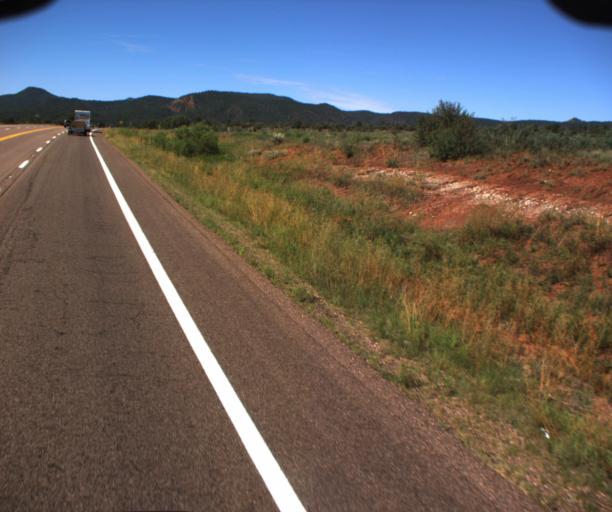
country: US
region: Arizona
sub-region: Navajo County
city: Cibecue
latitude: 33.9679
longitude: -110.3198
